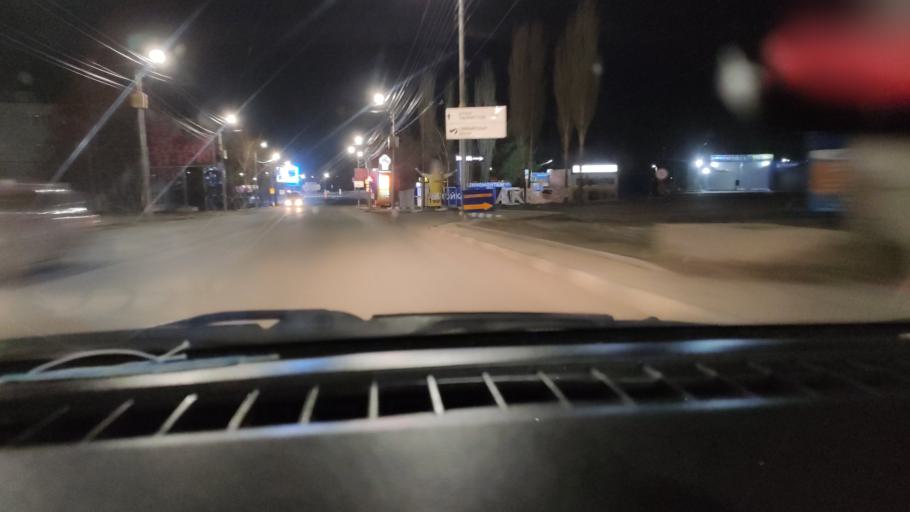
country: RU
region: Saratov
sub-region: Saratovskiy Rayon
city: Saratov
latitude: 51.5570
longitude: 46.0445
